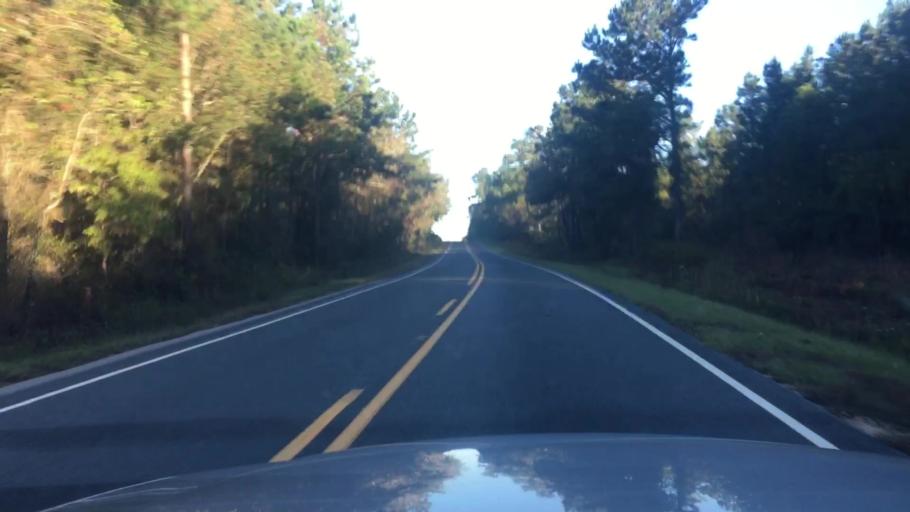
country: US
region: North Carolina
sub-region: Harnett County
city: Walkertown
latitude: 35.2779
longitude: -78.8648
